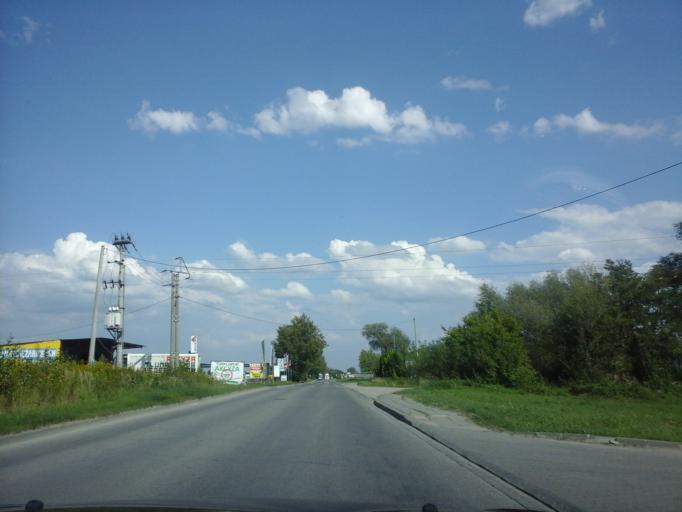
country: PL
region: Lesser Poland Voivodeship
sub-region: Powiat wielicki
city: Czarnochowice
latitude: 50.0331
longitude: 20.0459
